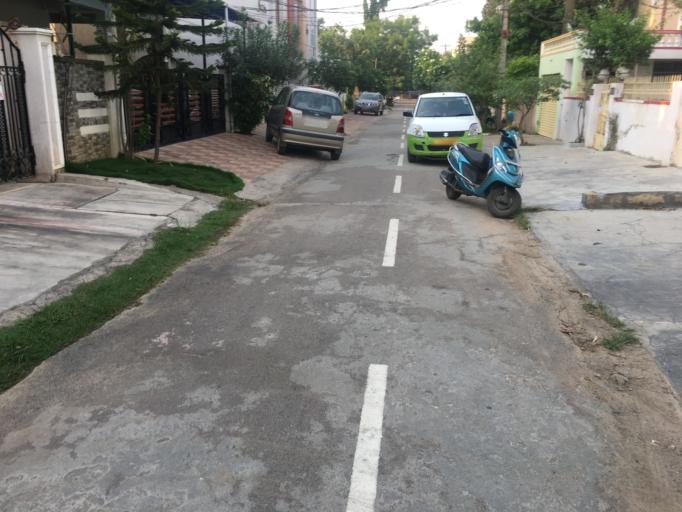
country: IN
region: Telangana
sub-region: Medak
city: Serilingampalle
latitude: 17.5056
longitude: 78.3029
